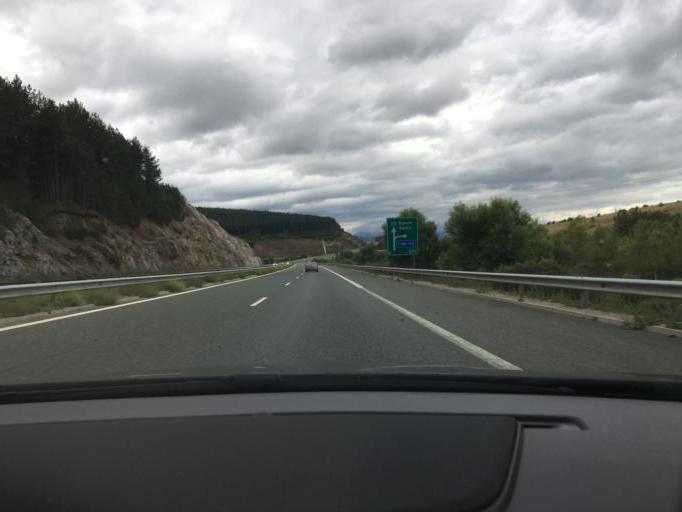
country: BG
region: Pernik
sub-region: Obshtina Pernik
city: Pernik
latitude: 42.4872
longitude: 23.1253
